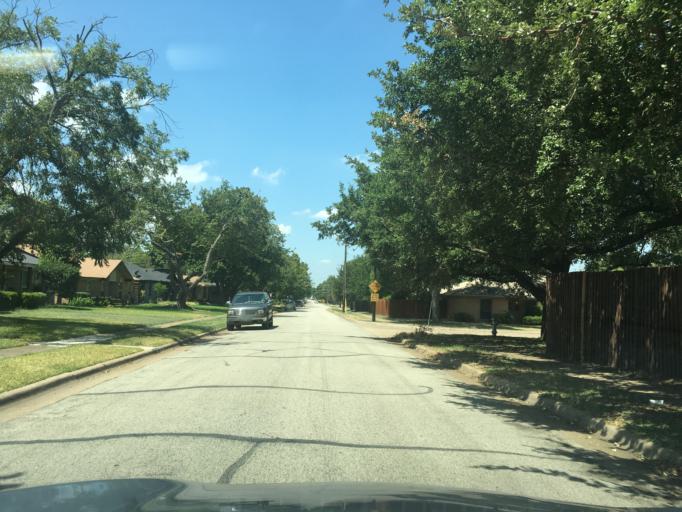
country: US
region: Texas
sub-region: Dallas County
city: Garland
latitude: 32.8694
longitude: -96.6854
